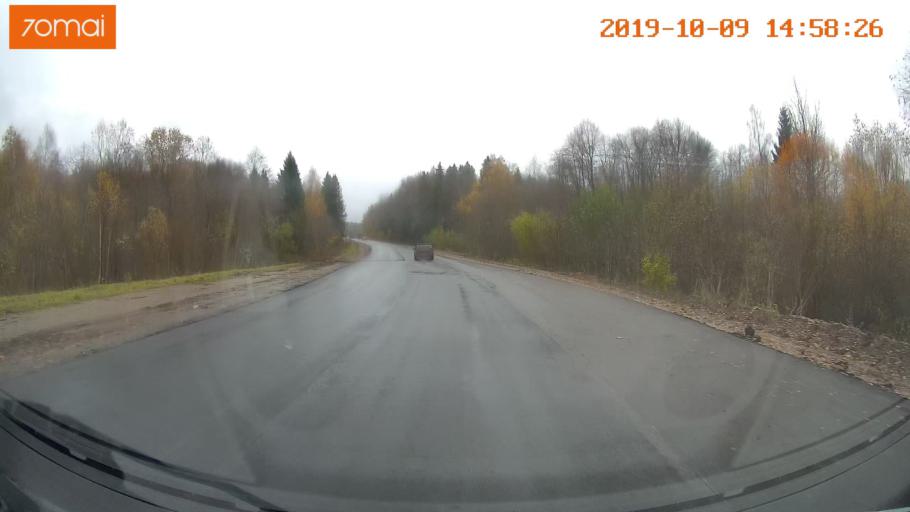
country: RU
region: Kostroma
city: Chistyye Bory
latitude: 58.3268
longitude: 41.6549
